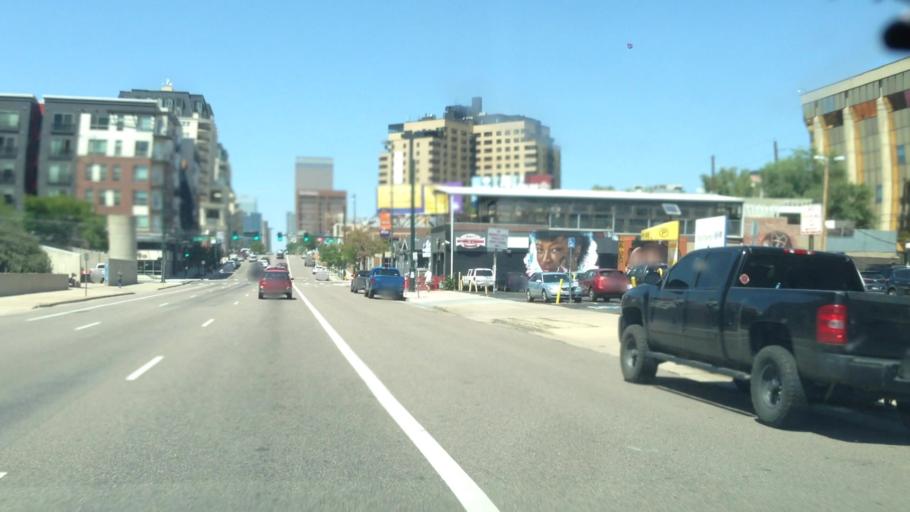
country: US
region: Colorado
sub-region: Denver County
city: Denver
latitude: 39.7280
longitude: -104.9861
